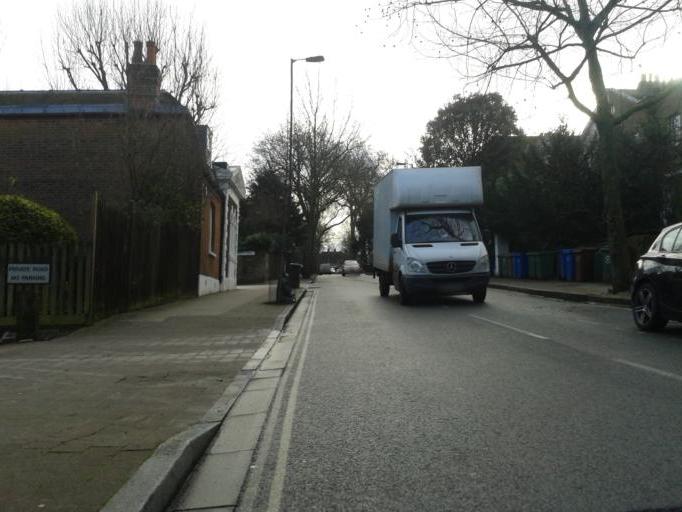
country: GB
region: England
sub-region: Greater London
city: Camberwell
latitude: 51.4679
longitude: -0.0845
